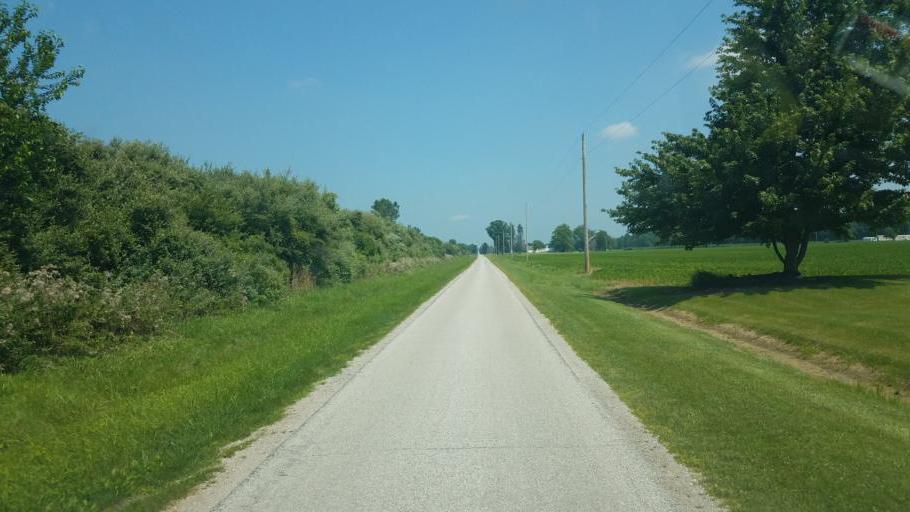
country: US
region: Ohio
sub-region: Seneca County
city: Tiffin
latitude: 41.0623
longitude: -82.9770
